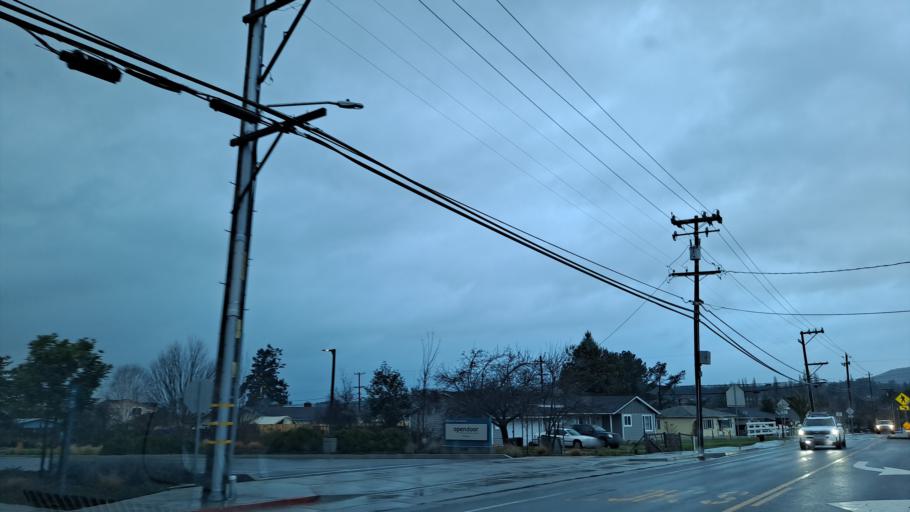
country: US
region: California
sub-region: Humboldt County
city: Fortuna
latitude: 40.5819
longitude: -124.1307
